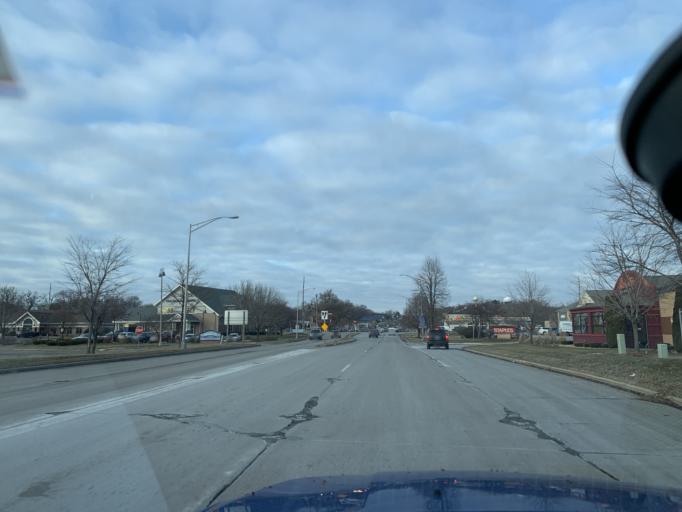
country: US
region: Wisconsin
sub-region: Dane County
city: Monona
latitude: 43.0462
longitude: -89.3243
